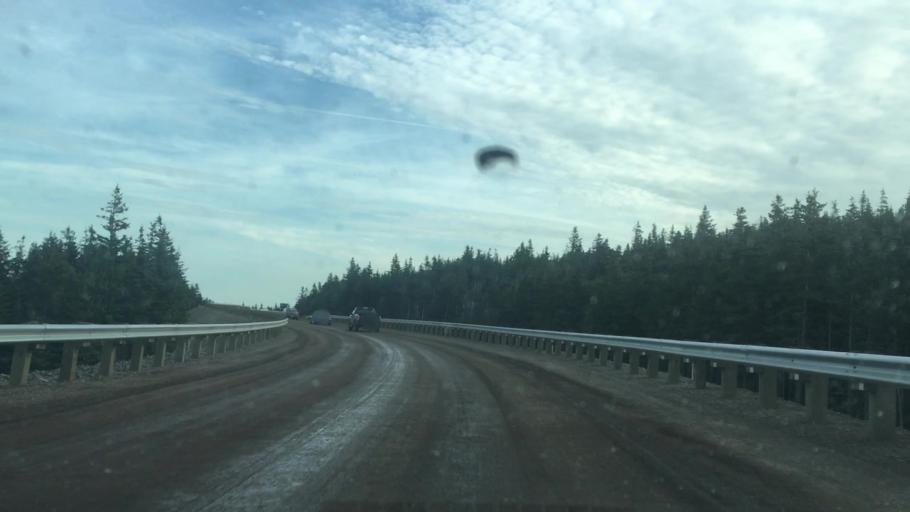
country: CA
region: Nova Scotia
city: Sydney Mines
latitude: 46.8060
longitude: -60.8443
